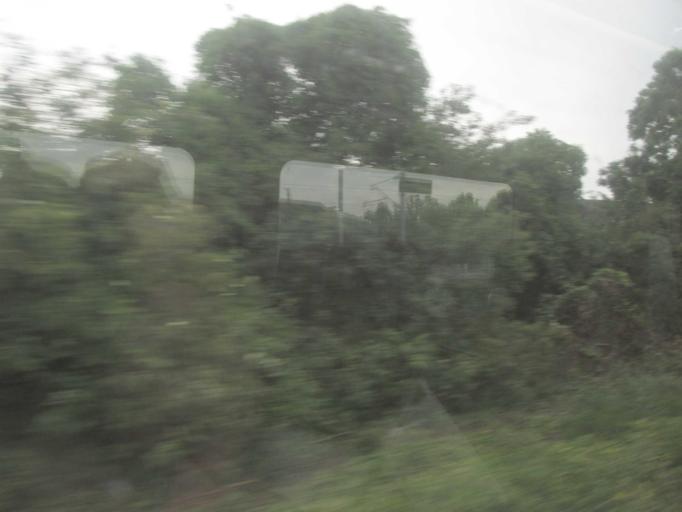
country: GB
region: England
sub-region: Bedford
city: Bedford
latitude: 52.1372
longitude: -0.4807
